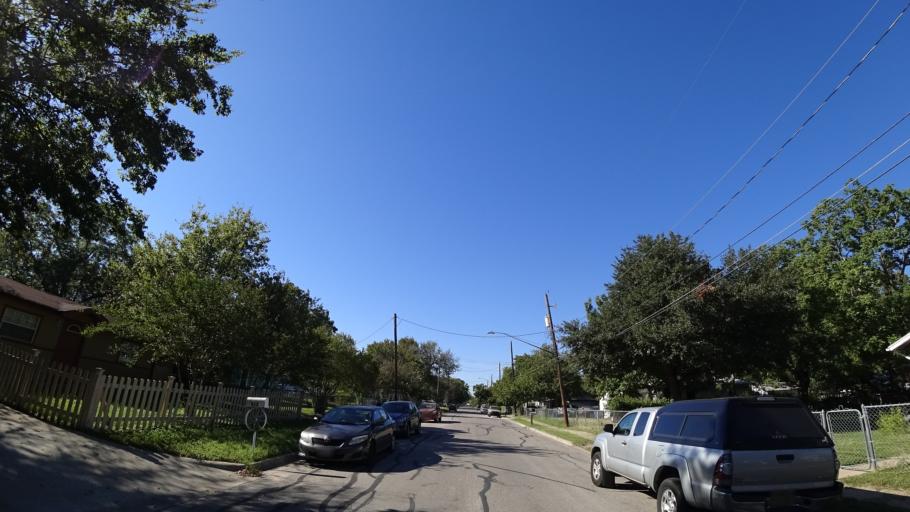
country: US
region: Texas
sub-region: Travis County
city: Austin
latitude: 30.2326
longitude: -97.6936
